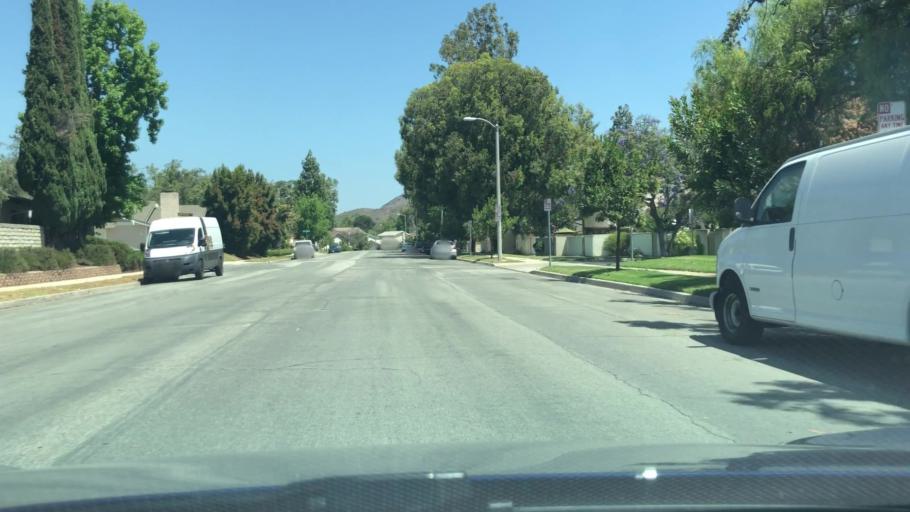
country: US
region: California
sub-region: Ventura County
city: Casa Conejo
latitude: 34.1804
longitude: -118.9556
